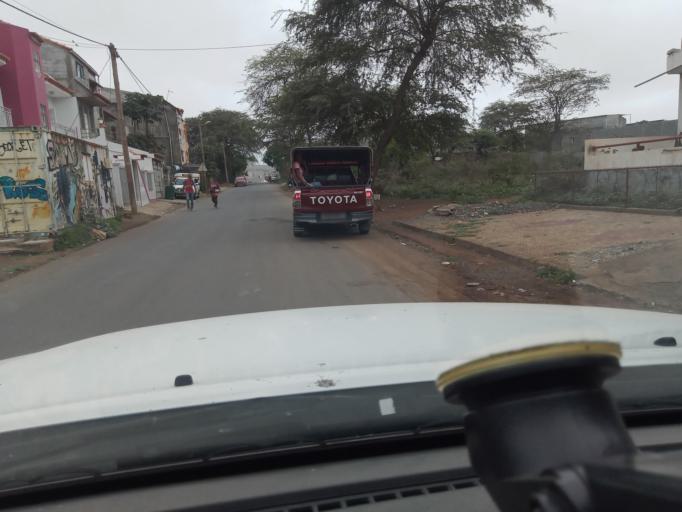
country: CV
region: Santa Catarina
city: Assomada
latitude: 15.1268
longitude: -23.6740
